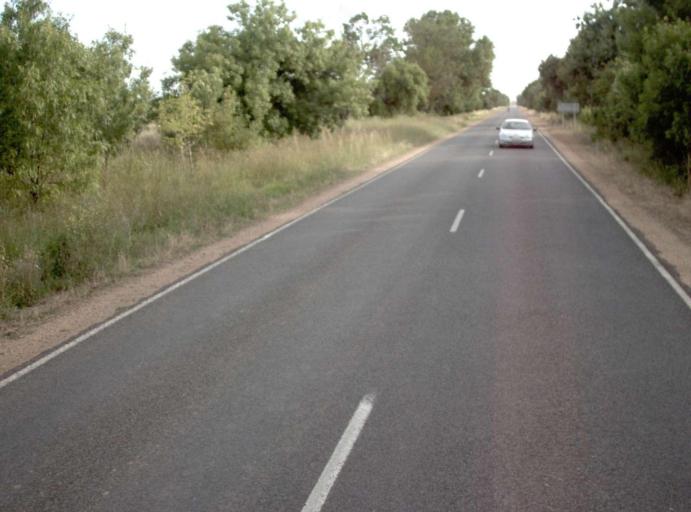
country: AU
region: Victoria
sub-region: Wellington
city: Heyfield
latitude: -37.9675
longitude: 146.8908
